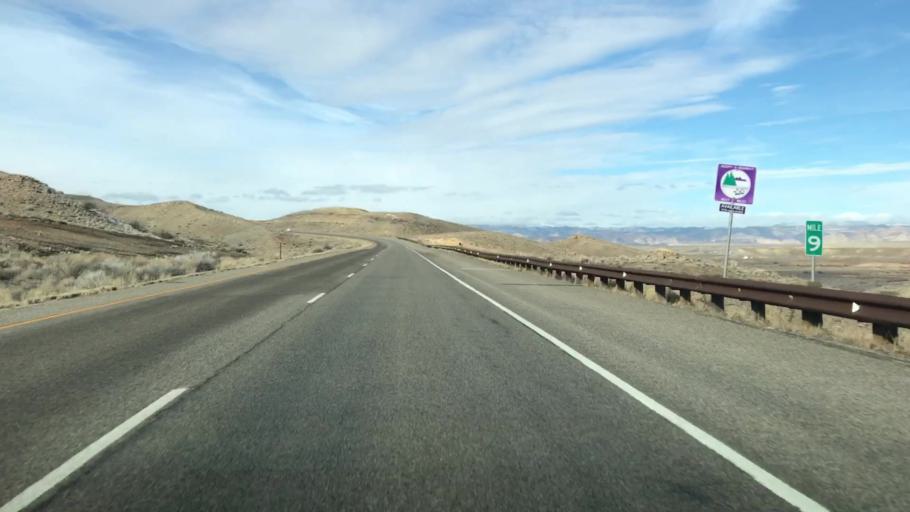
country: US
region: Colorado
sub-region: Mesa County
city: Loma
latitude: 39.2291
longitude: -108.9005
